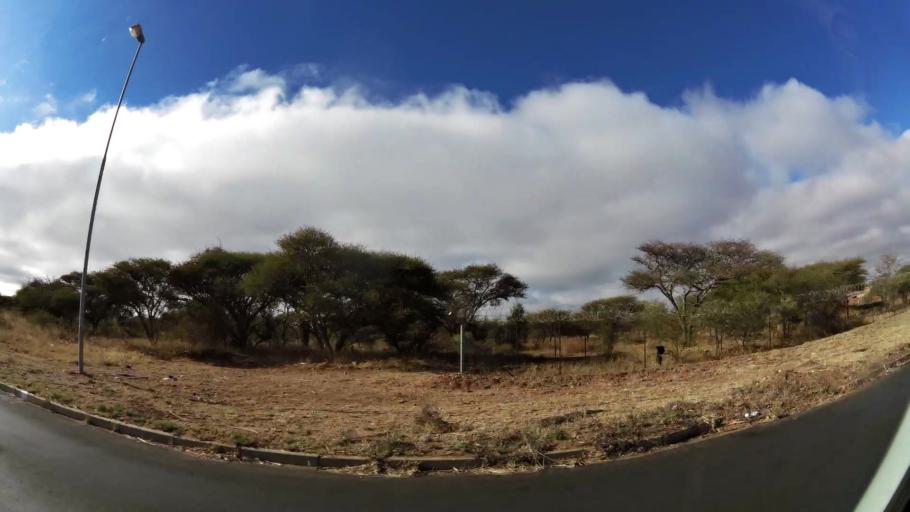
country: ZA
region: Limpopo
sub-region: Capricorn District Municipality
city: Polokwane
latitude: -23.9230
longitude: 29.4732
